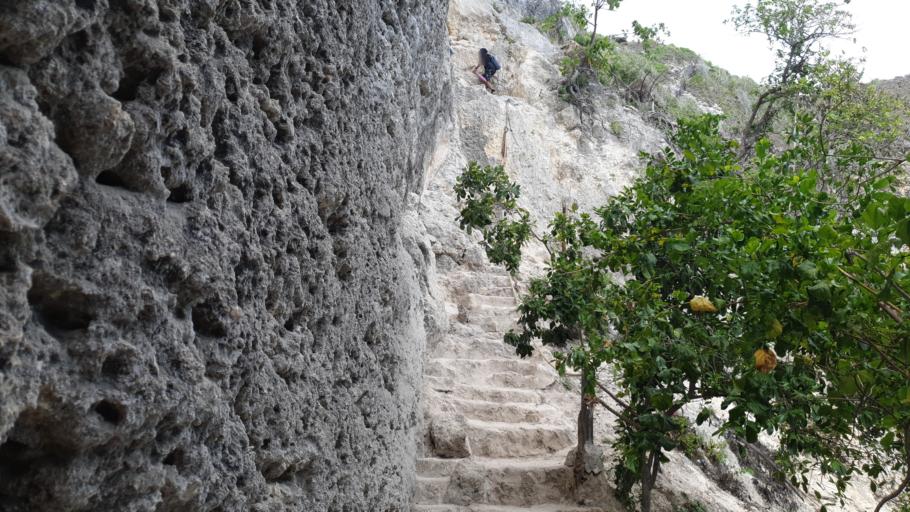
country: ID
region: Bali
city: Tanglad
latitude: -8.7750
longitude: 115.6200
